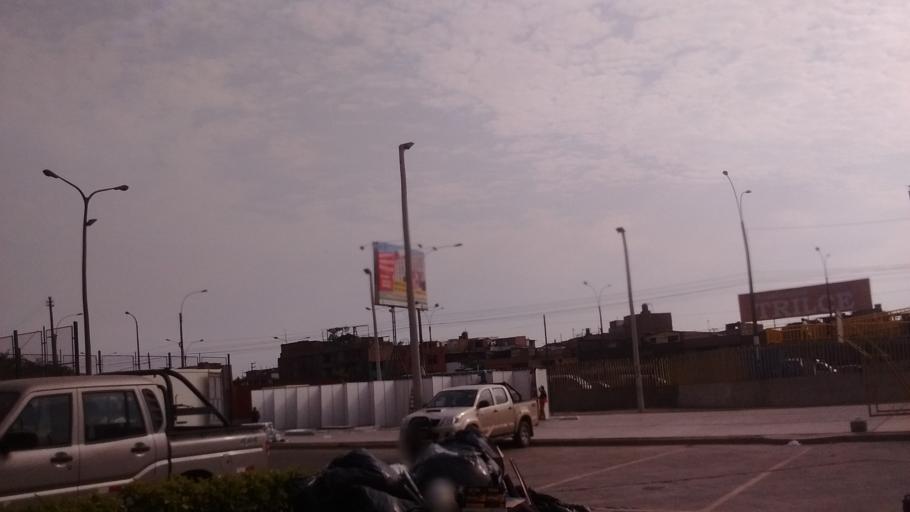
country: PE
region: Lima
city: Lima
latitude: -12.0245
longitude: -77.0474
